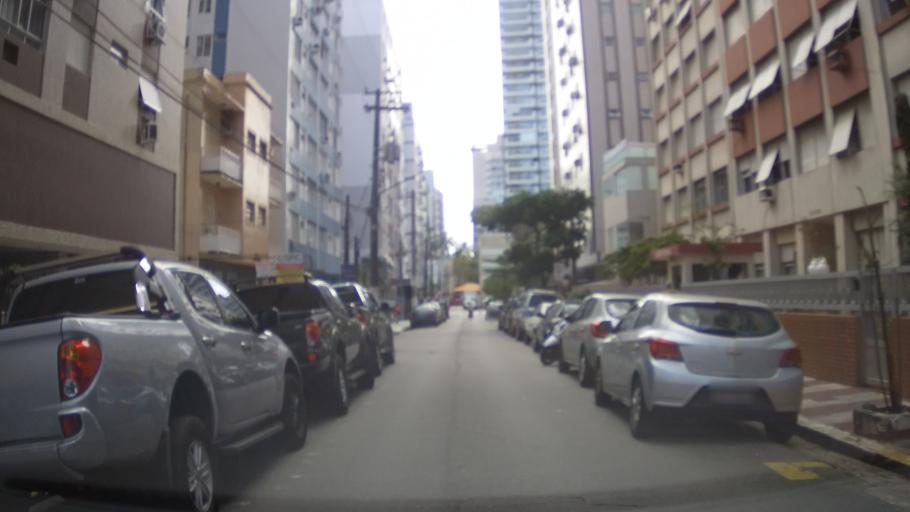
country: BR
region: Sao Paulo
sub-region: Santos
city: Santos
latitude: -23.9674
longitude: -46.3424
